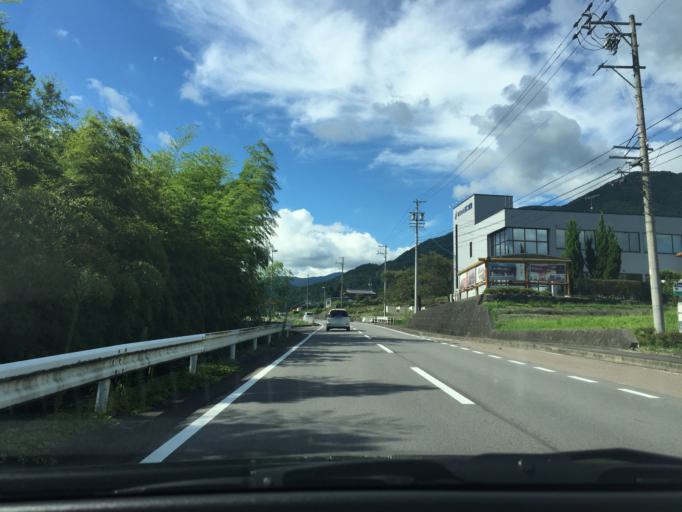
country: JP
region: Gifu
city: Nakatsugawa
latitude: 35.6547
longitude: 137.4343
